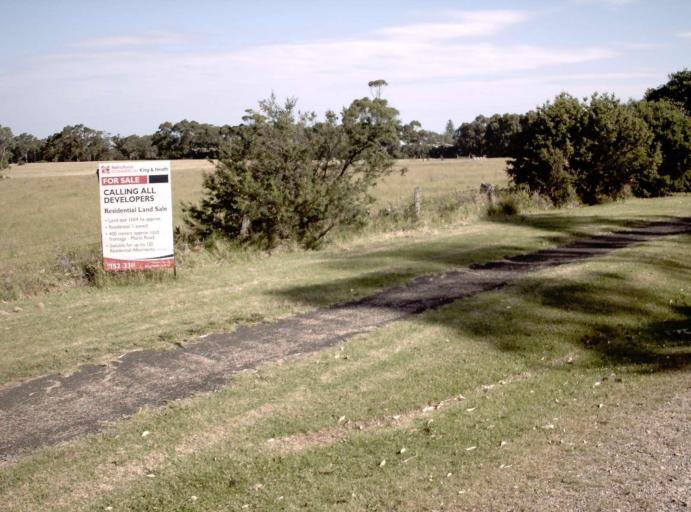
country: AU
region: Victoria
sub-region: East Gippsland
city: Lakes Entrance
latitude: -37.7920
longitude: 148.5348
